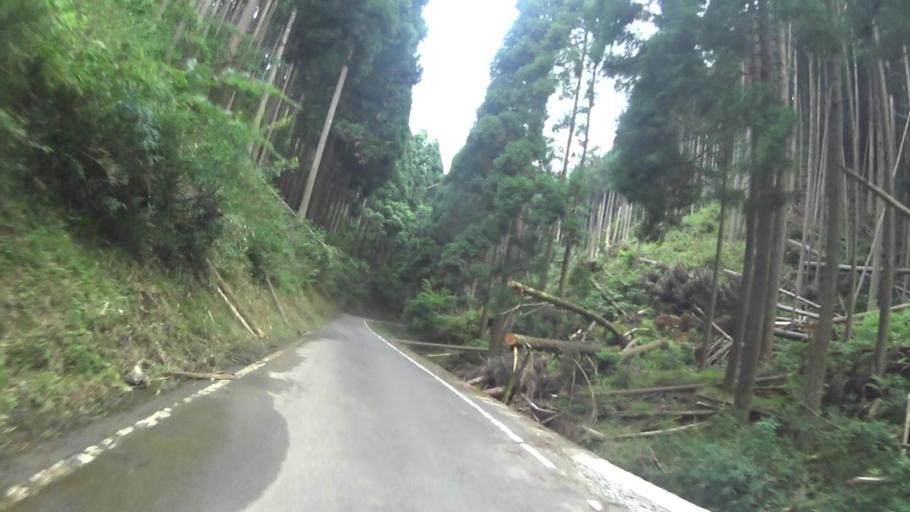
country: JP
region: Kyoto
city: Kameoka
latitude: 35.1625
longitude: 135.5735
